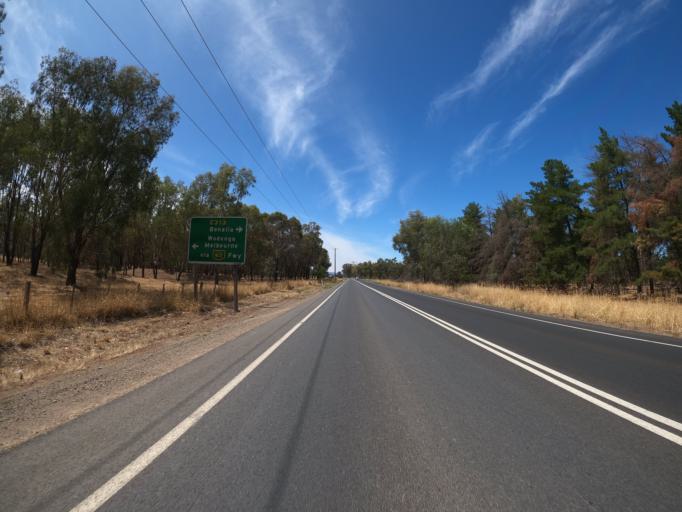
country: AU
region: Victoria
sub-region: Benalla
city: Benalla
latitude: -36.5277
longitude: 146.0396
